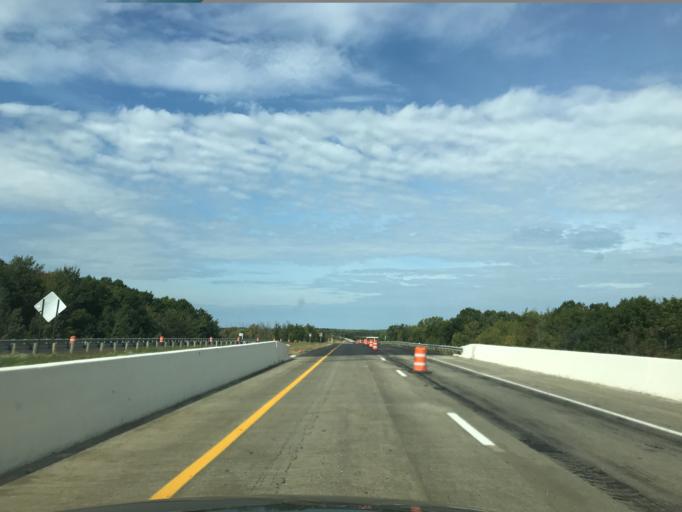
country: US
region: Ohio
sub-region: Ashtabula County
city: Jefferson
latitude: 41.8004
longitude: -80.7485
